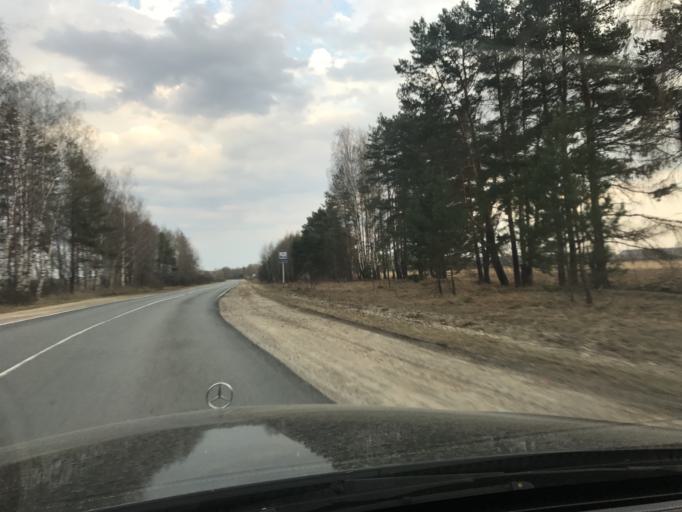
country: RU
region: Vladimir
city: Murom
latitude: 55.6326
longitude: 41.8776
